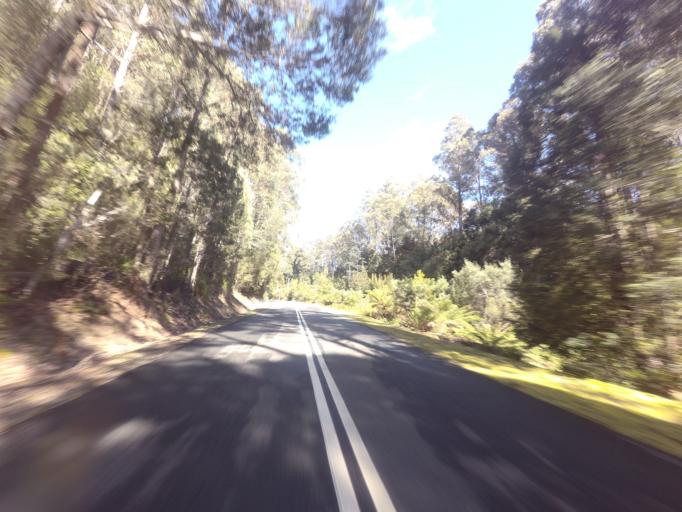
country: AU
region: Tasmania
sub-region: Derwent Valley
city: New Norfolk
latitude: -42.7511
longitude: 146.5191
